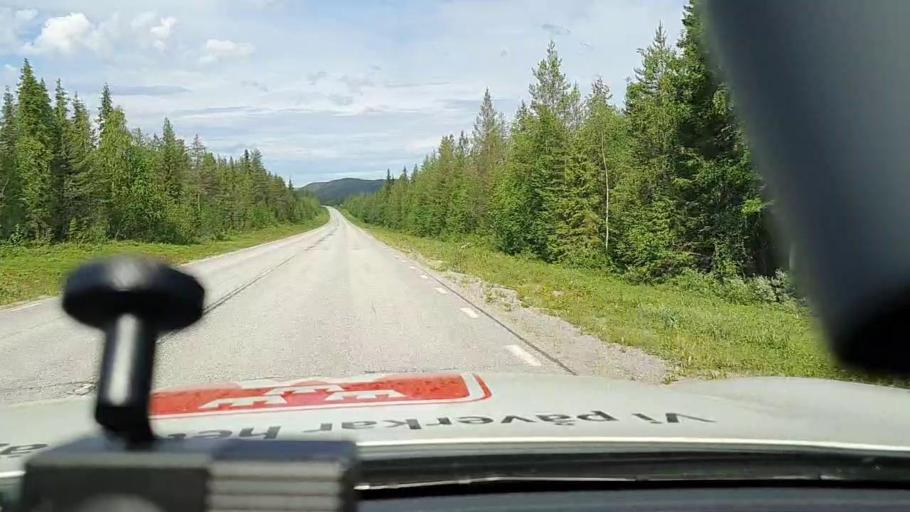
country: SE
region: Norrbotten
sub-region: Jokkmokks Kommun
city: Jokkmokk
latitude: 66.5468
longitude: 20.1313
